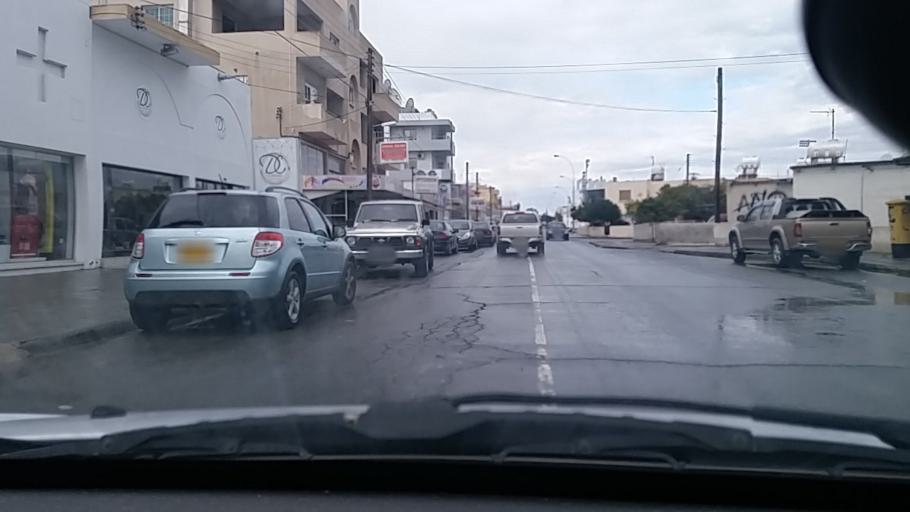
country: CY
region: Larnaka
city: Larnaca
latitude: 34.9342
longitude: 33.6218
